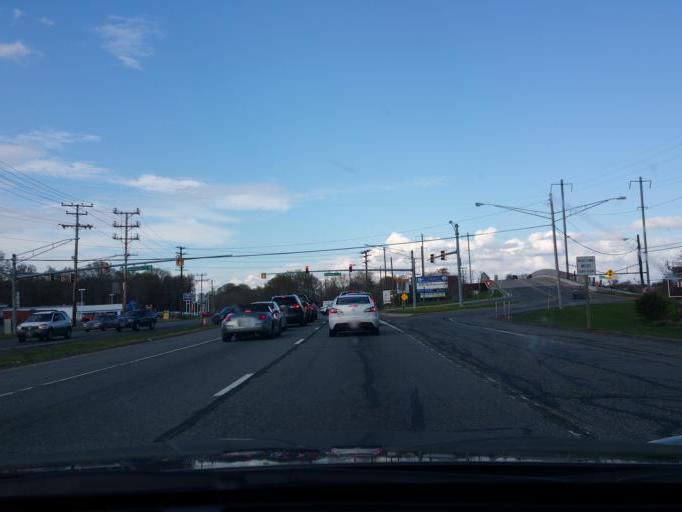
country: US
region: Maryland
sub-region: Harford County
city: Havre de Grace
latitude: 39.5353
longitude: -76.1162
